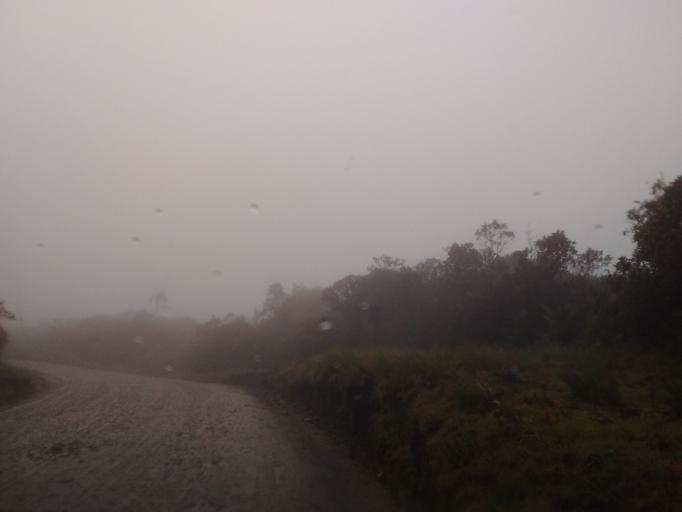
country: CO
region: Cauca
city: Paispamba
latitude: 2.1534
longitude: -76.4209
